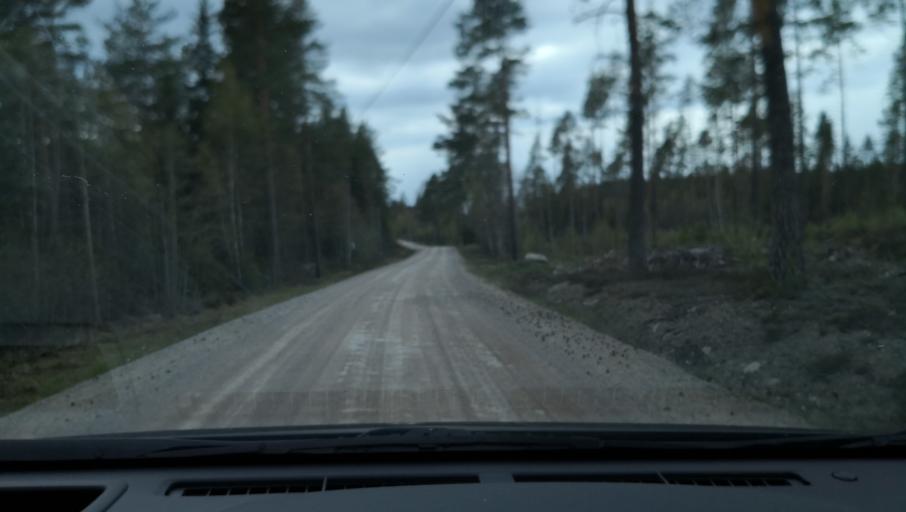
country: SE
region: Vaestmanland
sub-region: Norbergs Kommun
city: Norberg
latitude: 60.0907
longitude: 15.8430
